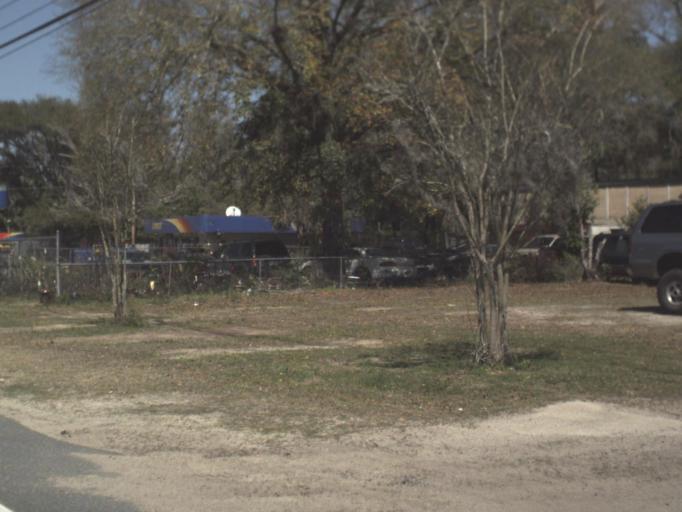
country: US
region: Florida
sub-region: Leon County
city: Tallahassee
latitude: 30.3973
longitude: -84.2796
